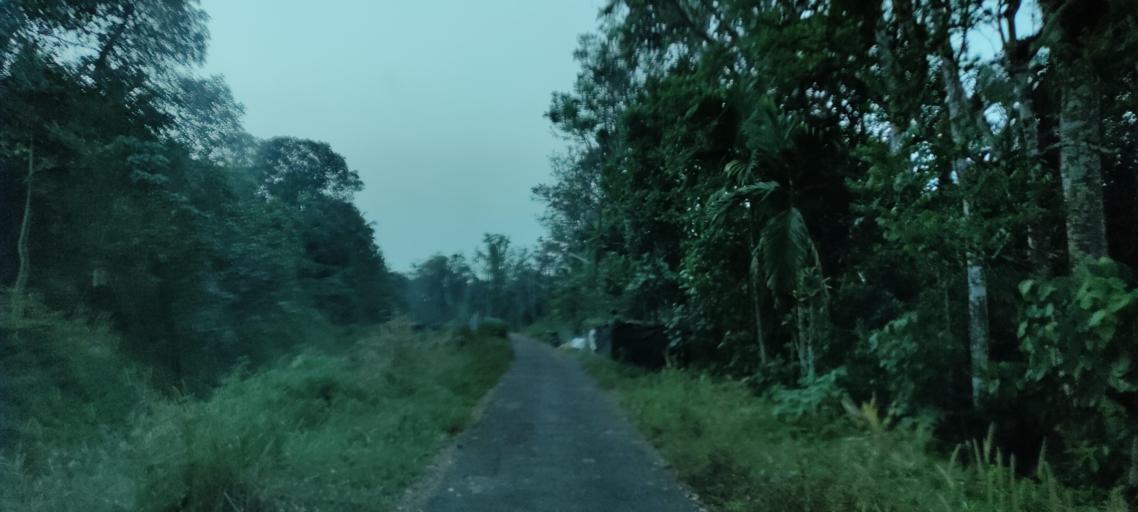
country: IN
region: Kerala
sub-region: Pattanamtitta
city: Adur
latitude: 9.1611
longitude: 76.7549
